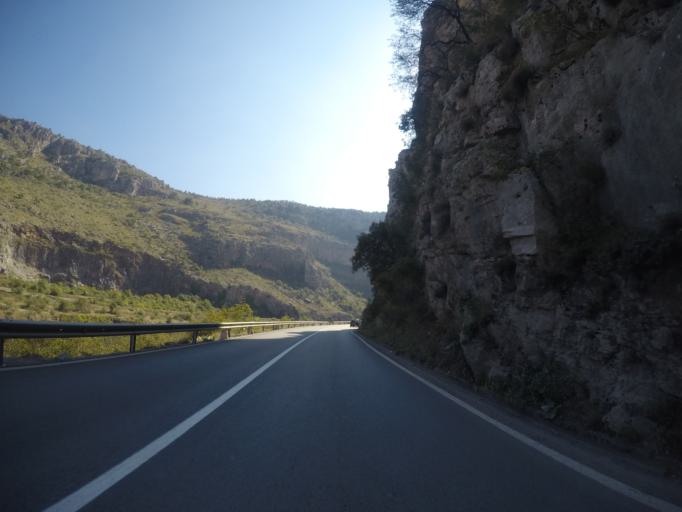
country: ME
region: Podgorica
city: Podgorica
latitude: 42.4888
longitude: 19.3086
